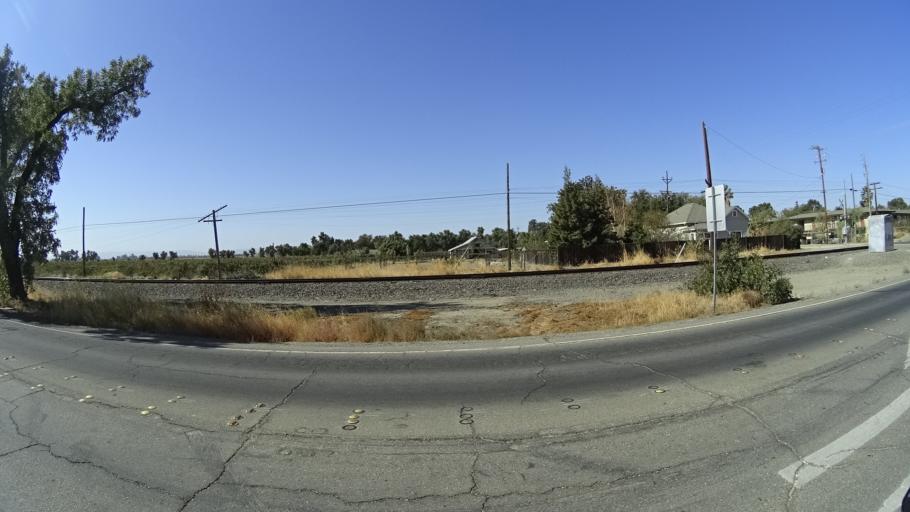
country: US
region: California
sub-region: Yolo County
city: Woodland
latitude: 38.6551
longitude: -121.7658
